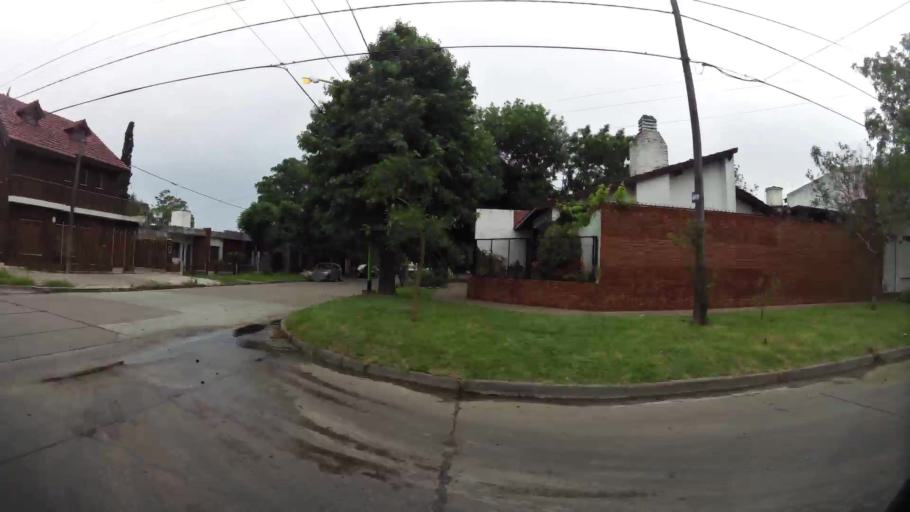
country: AR
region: Buenos Aires
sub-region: Partido de Campana
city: Campana
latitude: -34.1779
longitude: -58.9560
